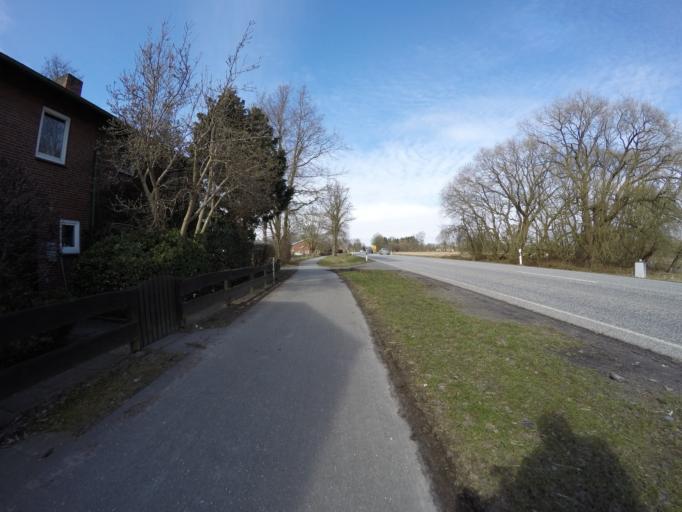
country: DE
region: Schleswig-Holstein
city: Bilsen
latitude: 53.7822
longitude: 9.8748
